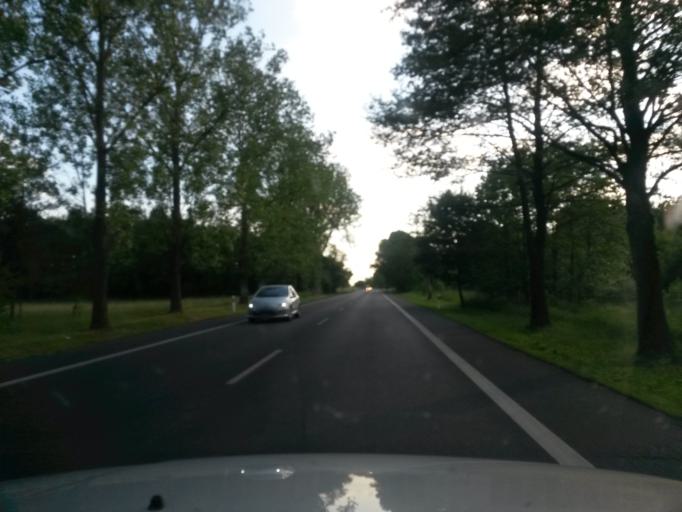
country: PL
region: Lodz Voivodeship
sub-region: Powiat wielunski
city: Osjakow
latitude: 51.3071
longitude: 18.8705
